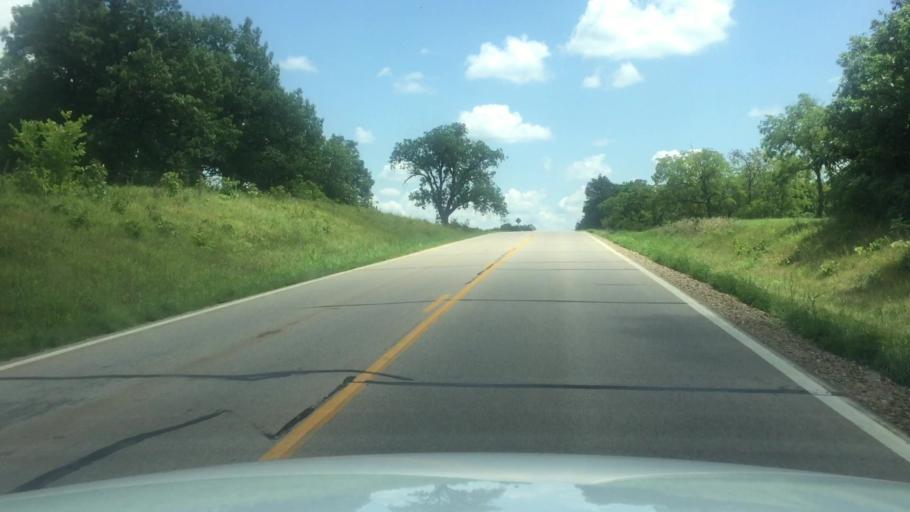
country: US
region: Kansas
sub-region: Brown County
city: Horton
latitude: 39.6674
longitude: -95.6340
